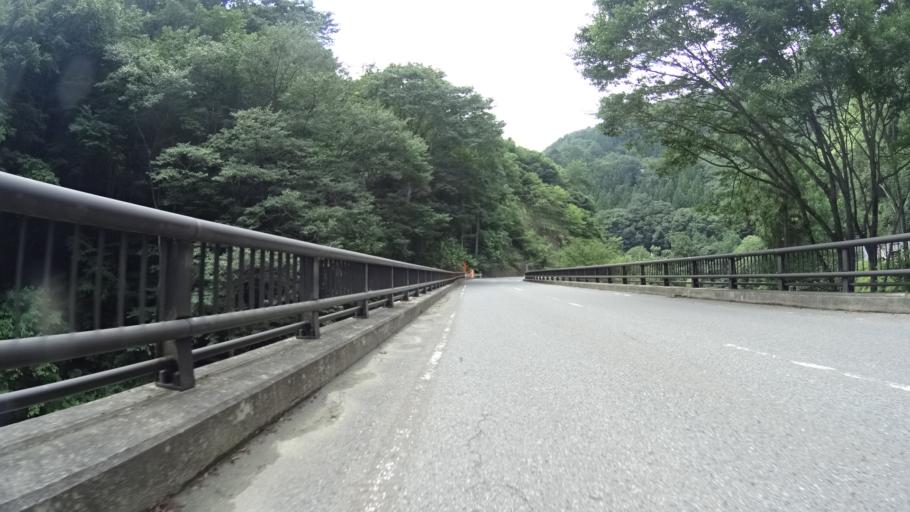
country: JP
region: Gunma
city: Tomioka
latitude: 36.0774
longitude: 138.7089
